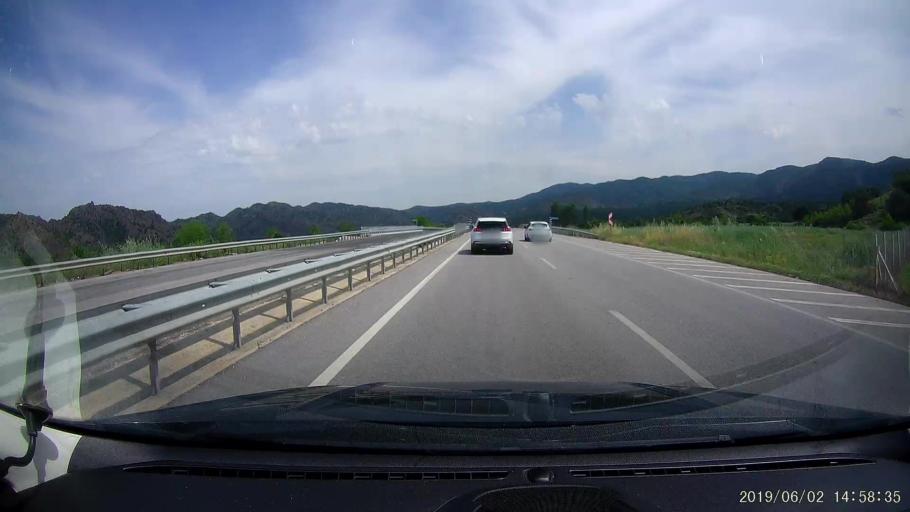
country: TR
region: Corum
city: Osmancik
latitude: 40.9801
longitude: 34.6799
